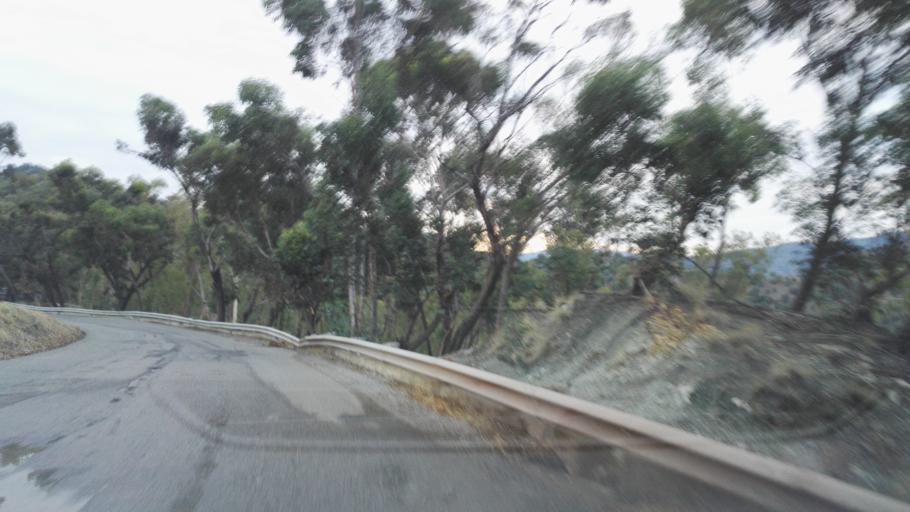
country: IT
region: Calabria
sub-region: Provincia di Reggio Calabria
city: Caulonia
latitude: 38.3849
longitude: 16.4027
